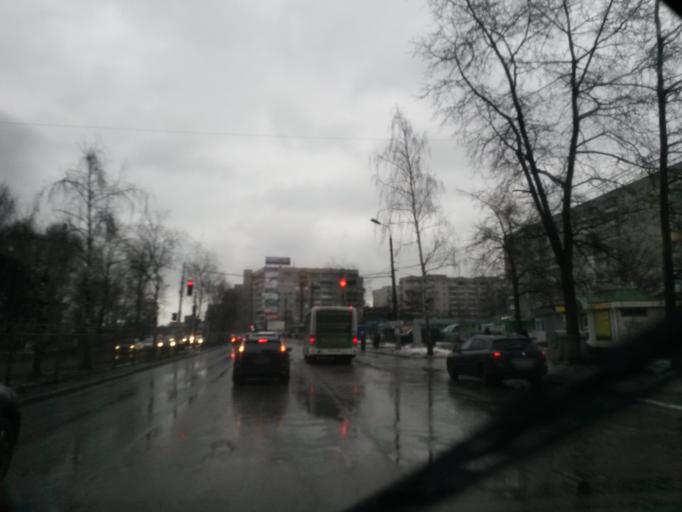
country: RU
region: Jaroslavl
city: Yaroslavl
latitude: 57.6536
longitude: 39.9395
